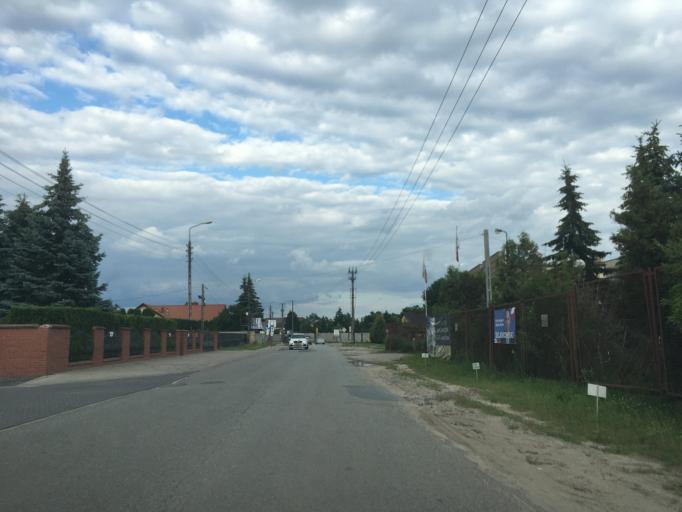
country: PL
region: Masovian Voivodeship
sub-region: Powiat piaseczynski
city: Mysiadlo
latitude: 52.1105
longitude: 21.0101
